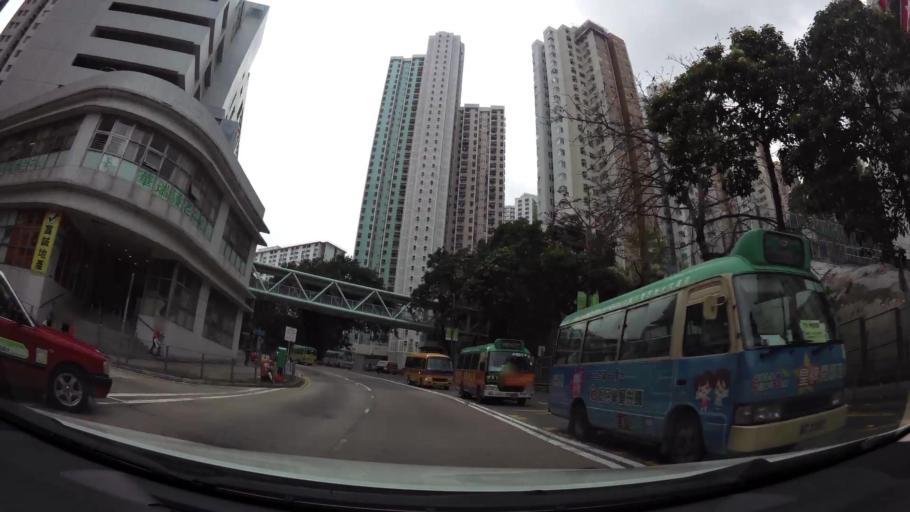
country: HK
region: Wong Tai Sin
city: Wong Tai Sin
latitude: 22.3406
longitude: 114.2081
